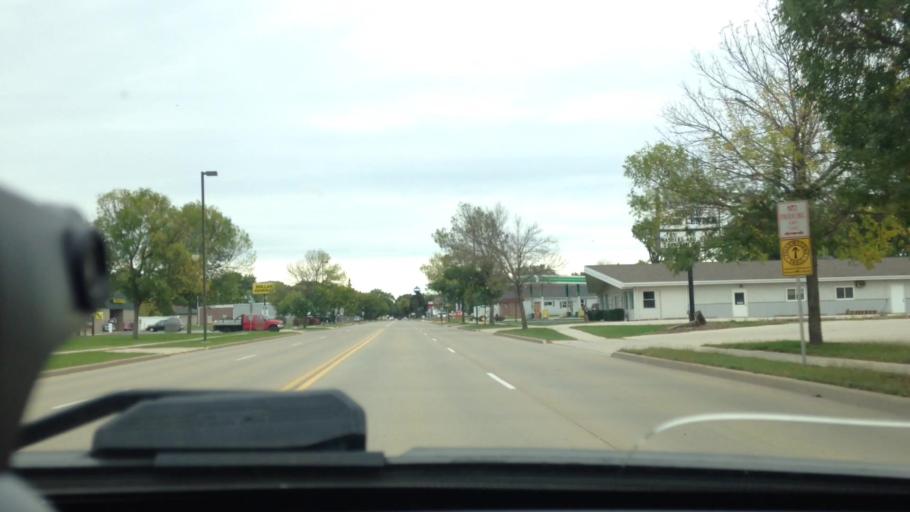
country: US
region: Wisconsin
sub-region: Fond du Lac County
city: North Fond du Lac
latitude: 43.8013
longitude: -88.4783
